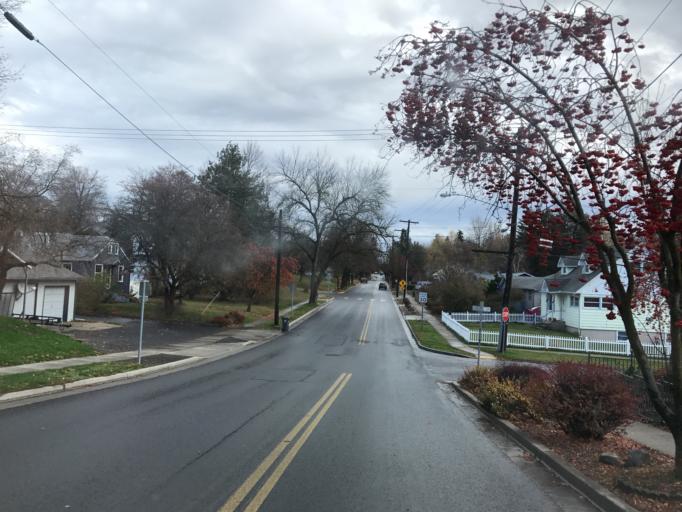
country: US
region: Idaho
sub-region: Latah County
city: Moscow
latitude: 46.7302
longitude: -116.9939
